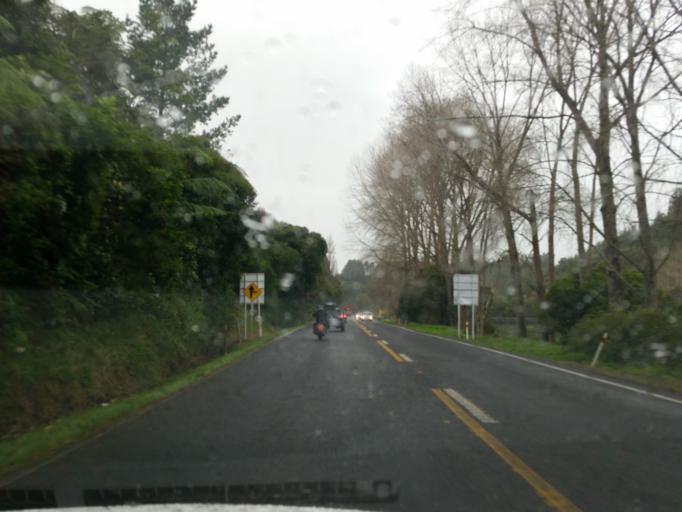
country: NZ
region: Waikato
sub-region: Hauraki District
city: Waihi
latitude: -37.4177
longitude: 175.7621
